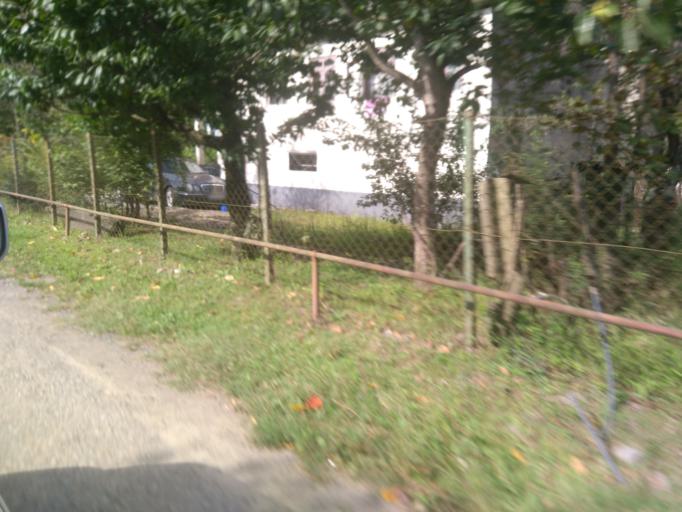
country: TR
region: Artvin
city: Muratli
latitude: 41.5471
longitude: 41.7610
